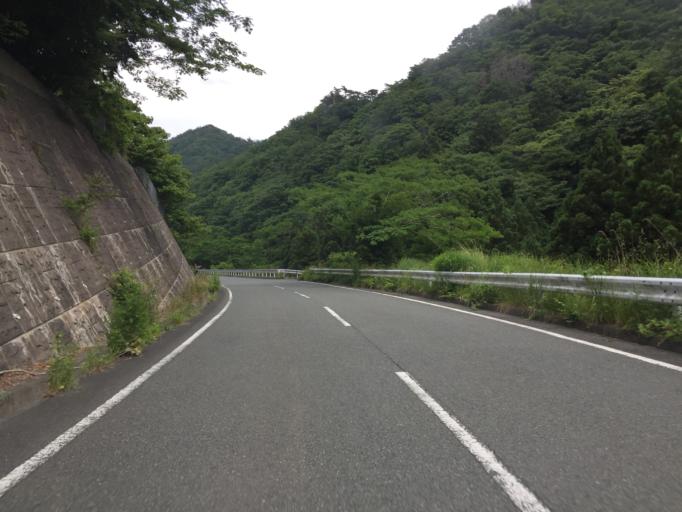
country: JP
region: Miyagi
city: Marumori
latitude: 37.8750
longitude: 140.8608
